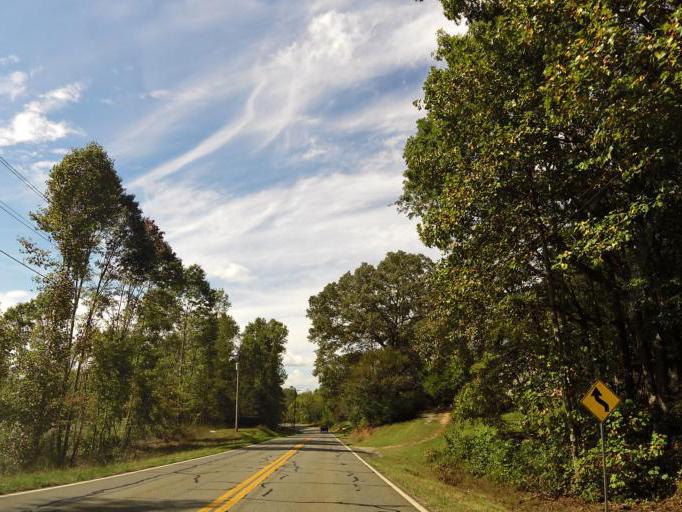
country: US
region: Georgia
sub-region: Pickens County
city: Nelson
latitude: 34.4166
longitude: -84.3005
